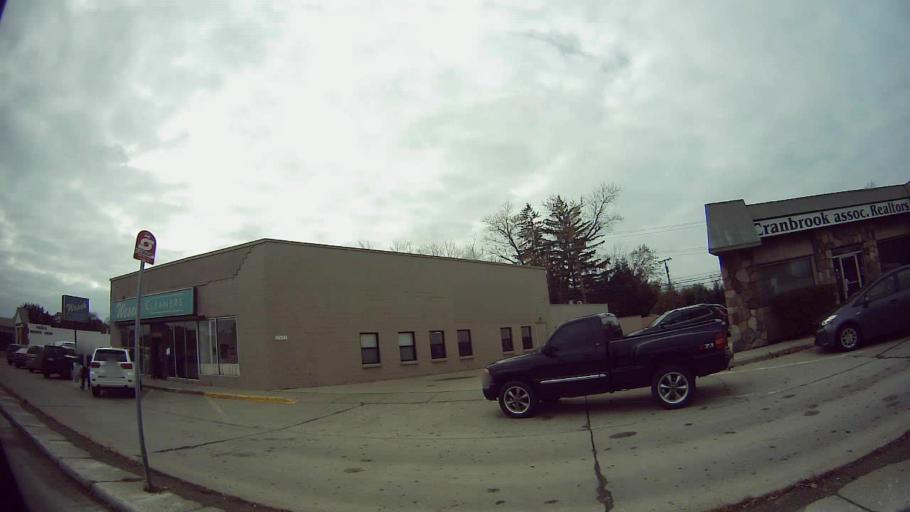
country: US
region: Michigan
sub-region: Oakland County
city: Birmingham
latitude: 42.5365
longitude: -83.2044
